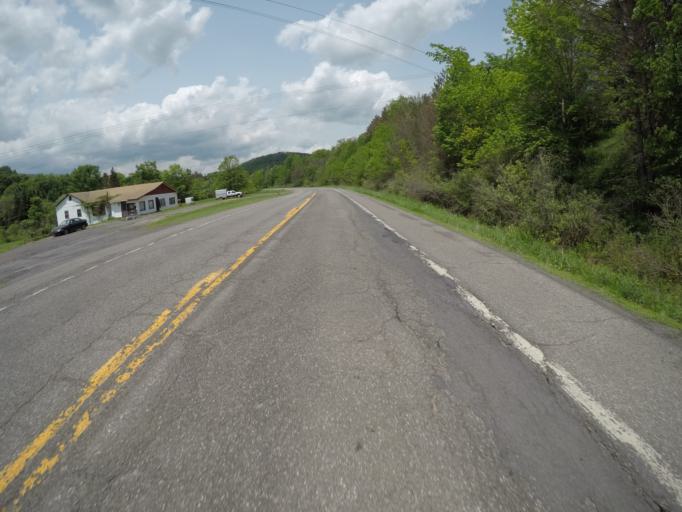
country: US
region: New York
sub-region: Delaware County
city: Stamford
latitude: 42.2234
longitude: -74.5919
